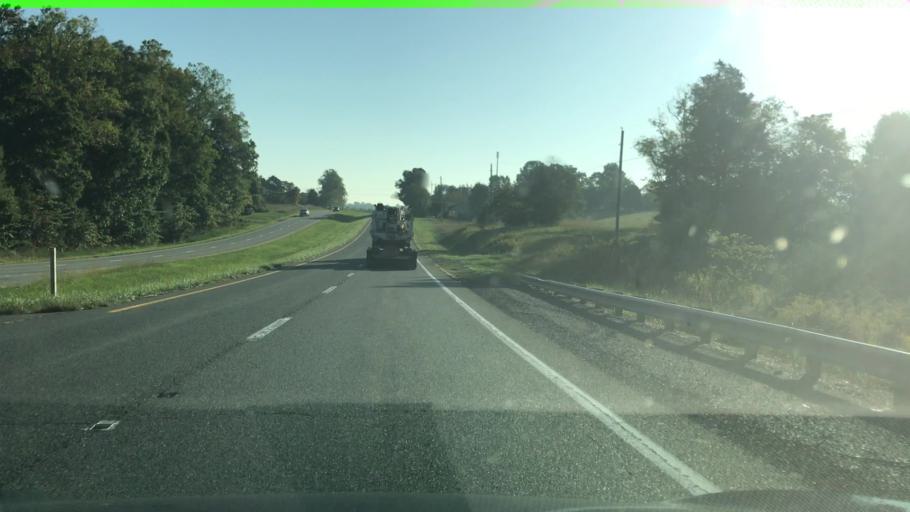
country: US
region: Virginia
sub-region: City of Bedford
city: Bedford
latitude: 37.3134
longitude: -79.4599
